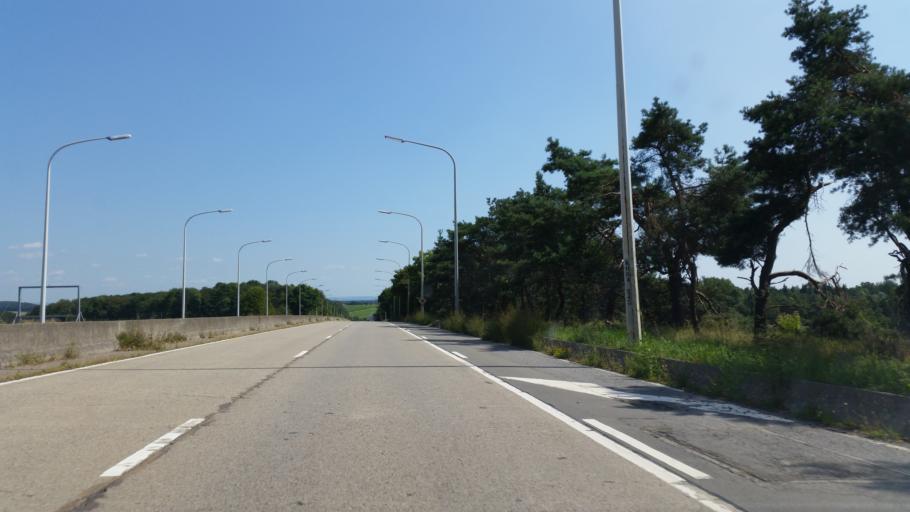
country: BE
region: Wallonia
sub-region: Province de Namur
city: Hamois
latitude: 50.2794
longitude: 5.2169
